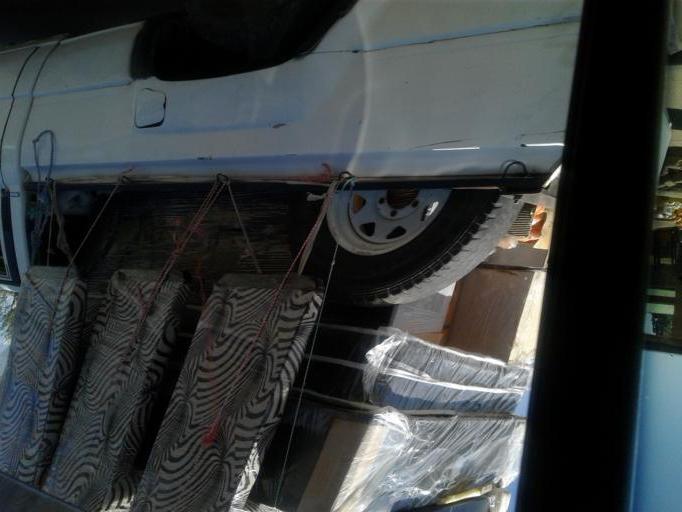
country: LS
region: Butha-Buthe
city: Butha-Buthe
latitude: -28.7673
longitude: 28.2531
